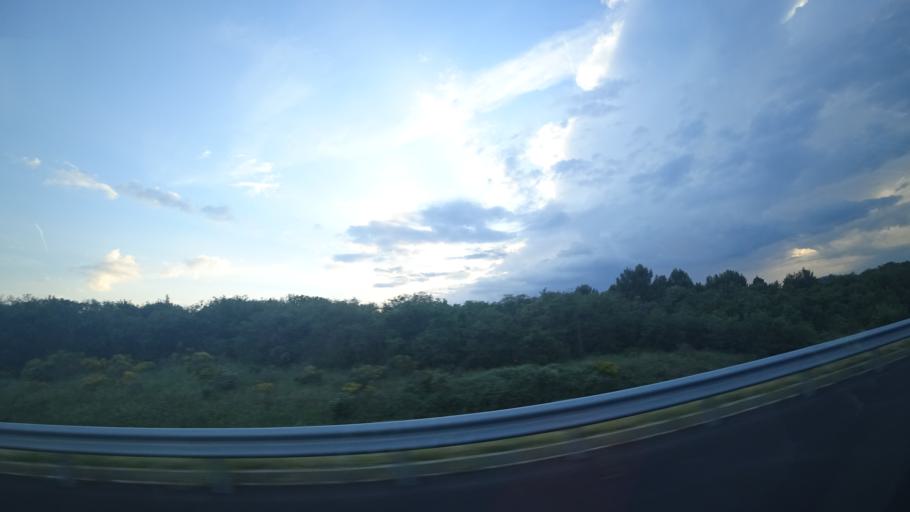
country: FR
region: Languedoc-Roussillon
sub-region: Departement de l'Herault
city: Paulhan
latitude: 43.5345
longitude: 3.4436
